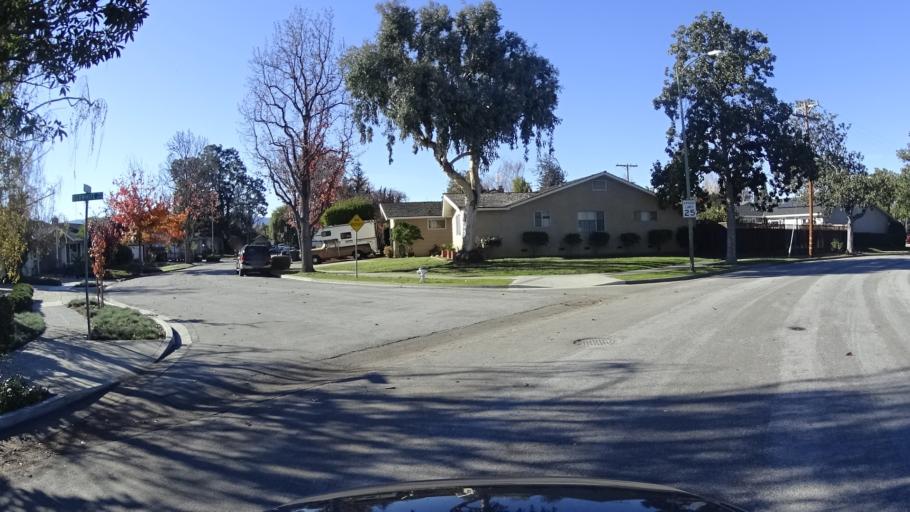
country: US
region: California
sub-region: Santa Clara County
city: Sunnyvale
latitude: 37.3470
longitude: -122.0272
